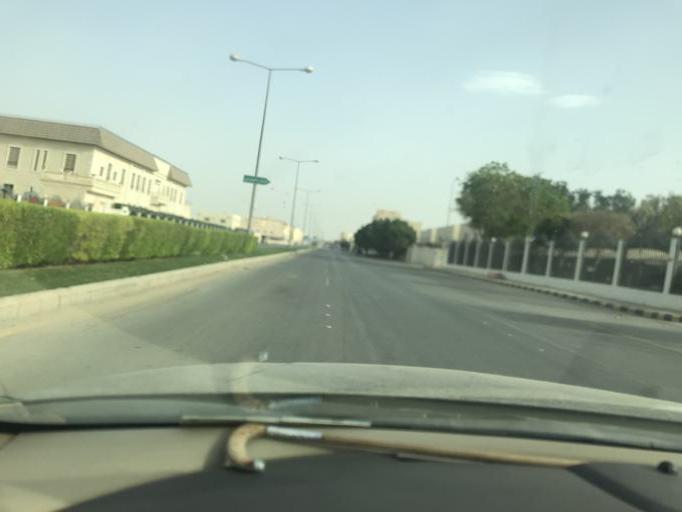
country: SA
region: Ar Riyad
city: Riyadh
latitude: 24.7876
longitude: 46.7126
